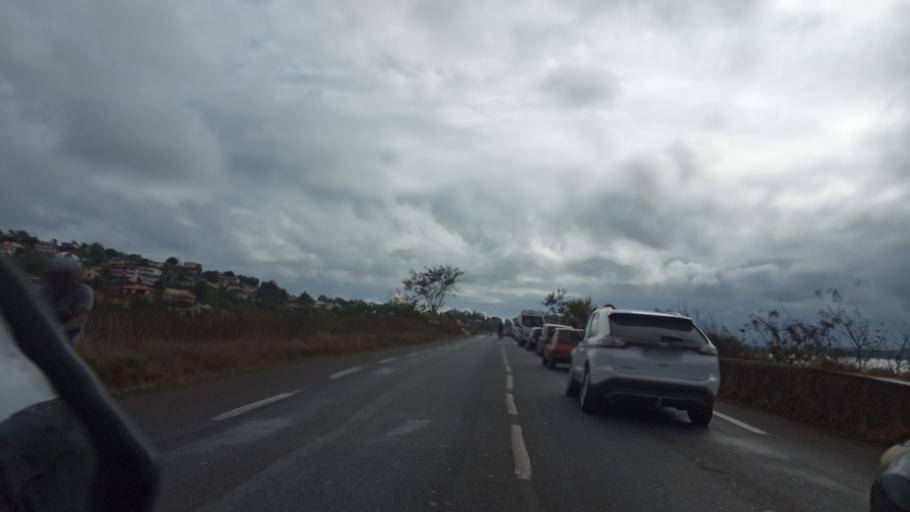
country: YT
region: Mamoudzou
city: Mamoudzou
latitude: -12.7918
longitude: 45.2215
